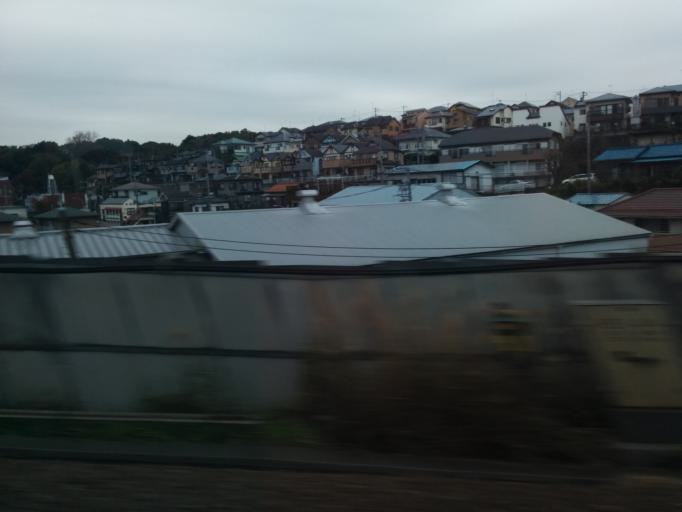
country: JP
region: Kanagawa
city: Yokohama
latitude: 35.4859
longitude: 139.5898
